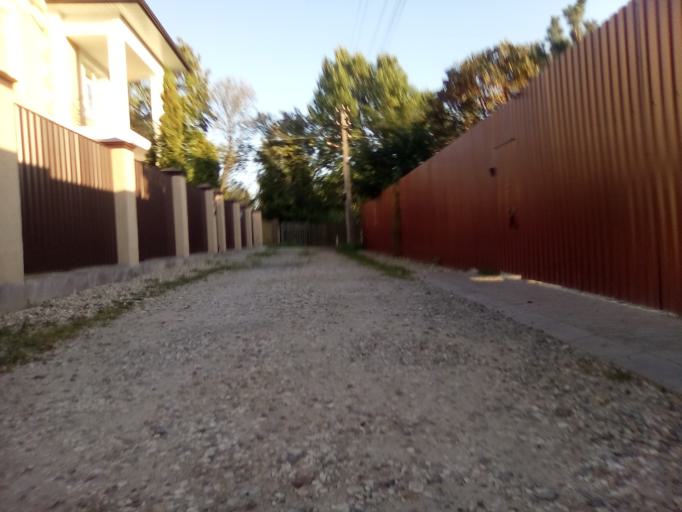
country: RU
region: Moskovskaya
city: Krasnoznamensk
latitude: 55.5787
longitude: 37.0406
